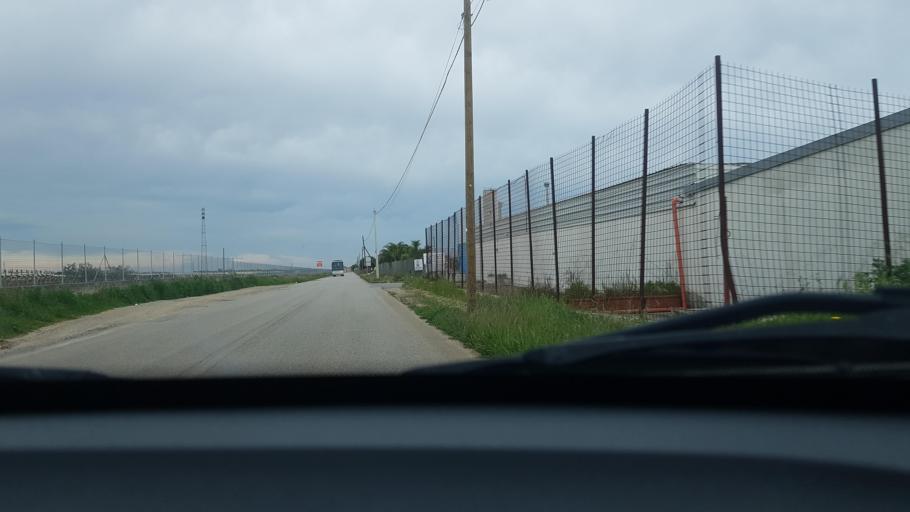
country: IT
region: Apulia
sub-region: Provincia di Bari
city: Noicattaro
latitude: 41.0347
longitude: 16.9749
